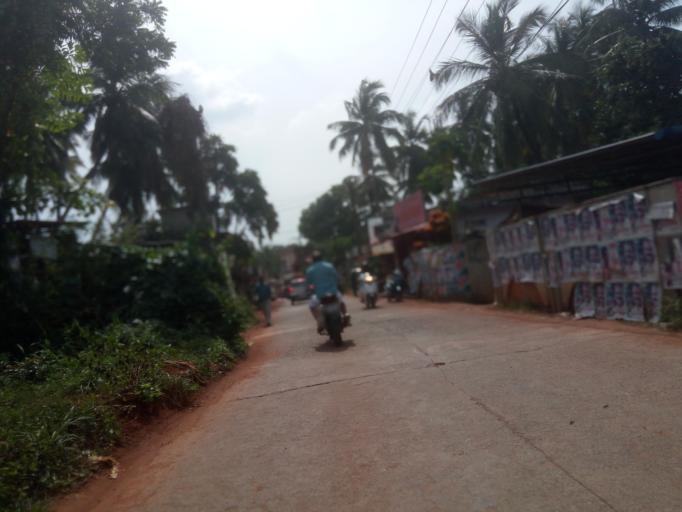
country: IN
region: Kerala
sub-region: Malappuram
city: Ponnani
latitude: 10.7866
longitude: 76.0254
